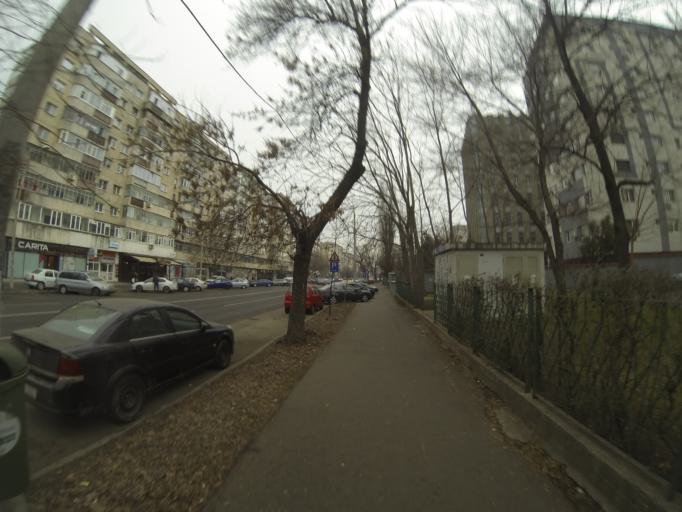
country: RO
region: Bucuresti
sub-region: Municipiul Bucuresti
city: Bucuresti
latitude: 44.4167
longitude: 26.0695
